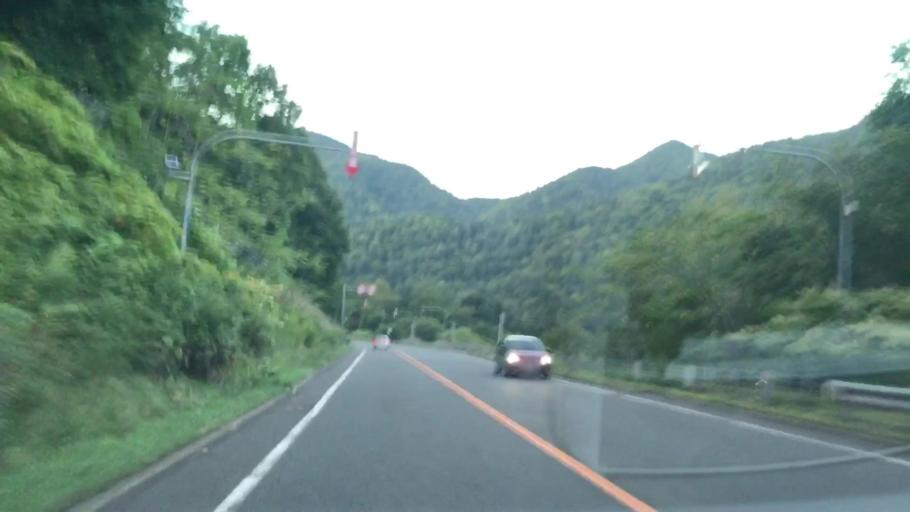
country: JP
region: Hokkaido
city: Sapporo
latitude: 42.9138
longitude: 141.1222
